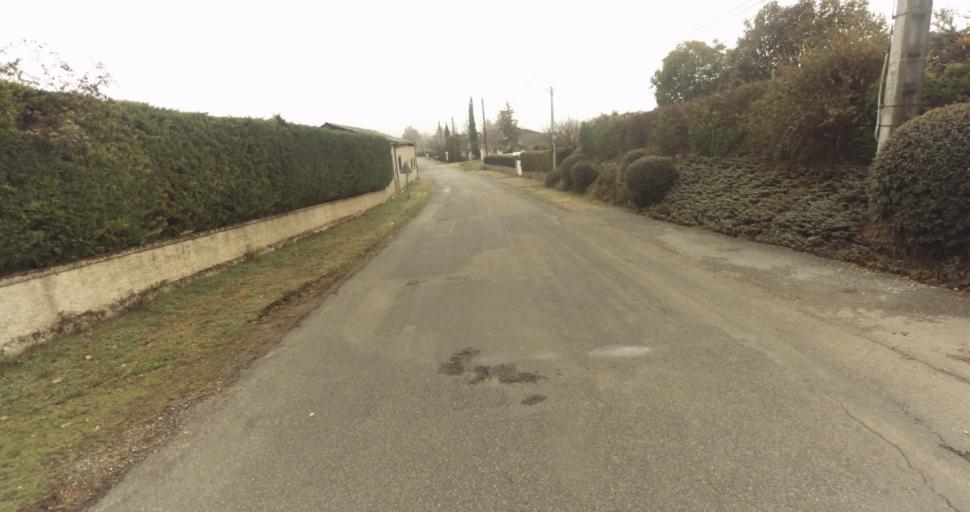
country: FR
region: Midi-Pyrenees
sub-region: Departement du Lot
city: Figeac
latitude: 44.6231
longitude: 2.0226
